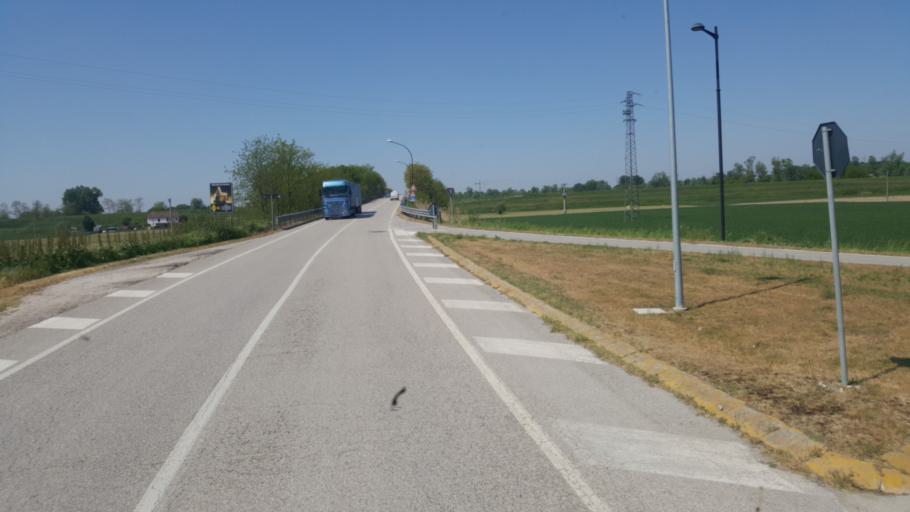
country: IT
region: Veneto
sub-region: Provincia di Rovigo
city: Ficarolo
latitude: 44.9446
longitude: 11.4334
